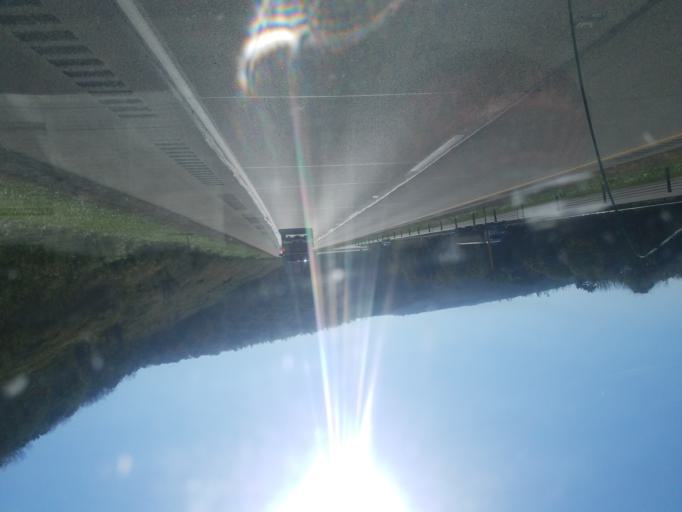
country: US
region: Pennsylvania
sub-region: Cambria County
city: Gallitzin
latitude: 40.4765
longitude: -78.5158
